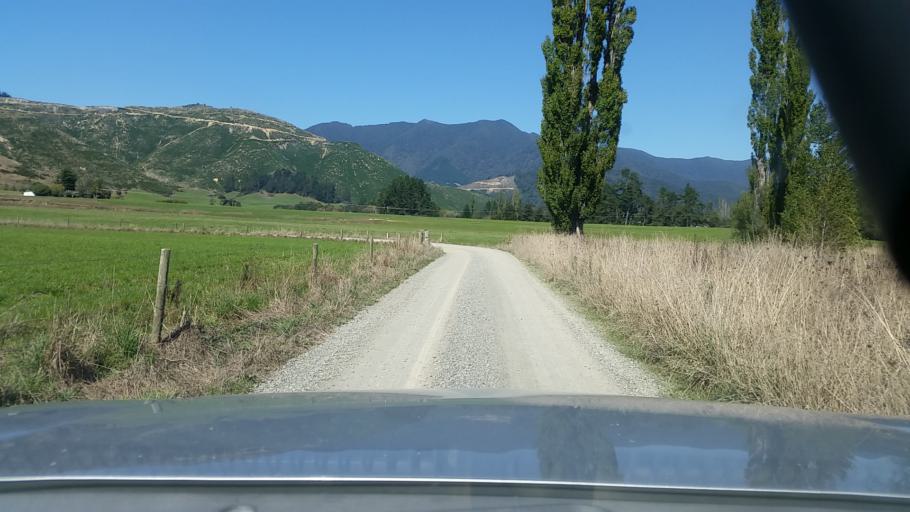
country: NZ
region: Nelson
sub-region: Nelson City
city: Nelson
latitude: -41.2690
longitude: 173.5755
